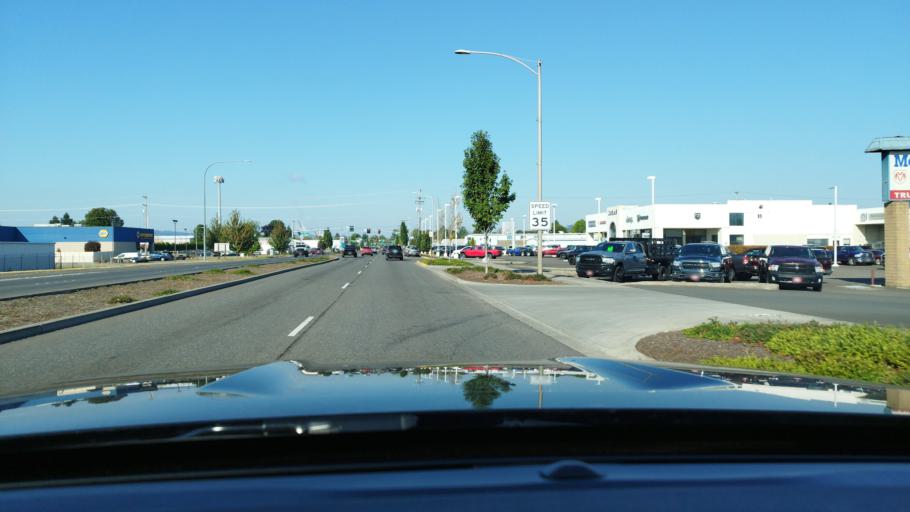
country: US
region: Washington
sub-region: Cowlitz County
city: Longview
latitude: 46.1245
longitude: -122.9313
